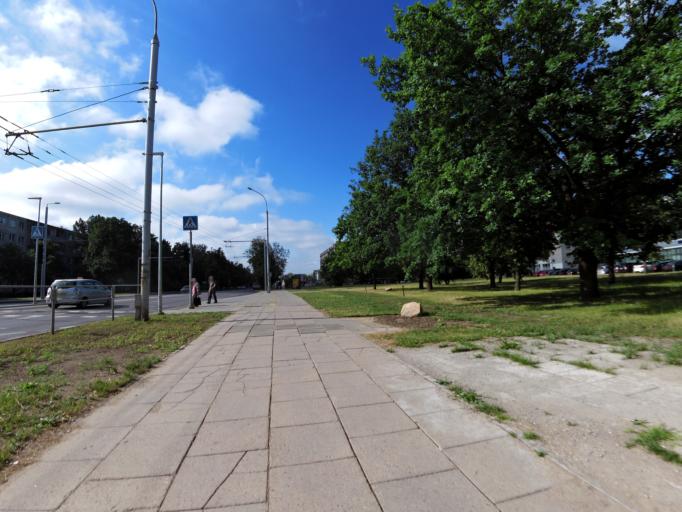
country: LT
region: Vilnius County
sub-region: Vilnius
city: Vilnius
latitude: 54.7163
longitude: 25.3051
